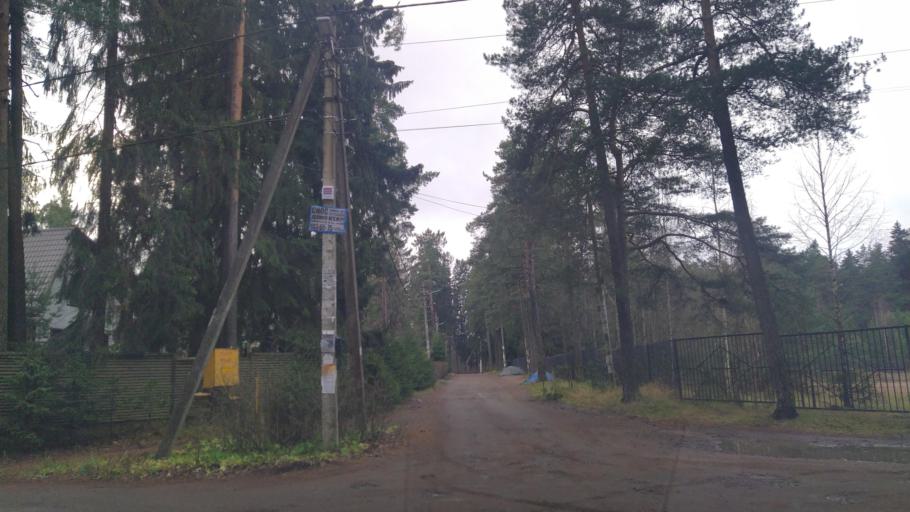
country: RU
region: Leningrad
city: Vsevolozhsk
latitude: 60.0222
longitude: 30.6718
